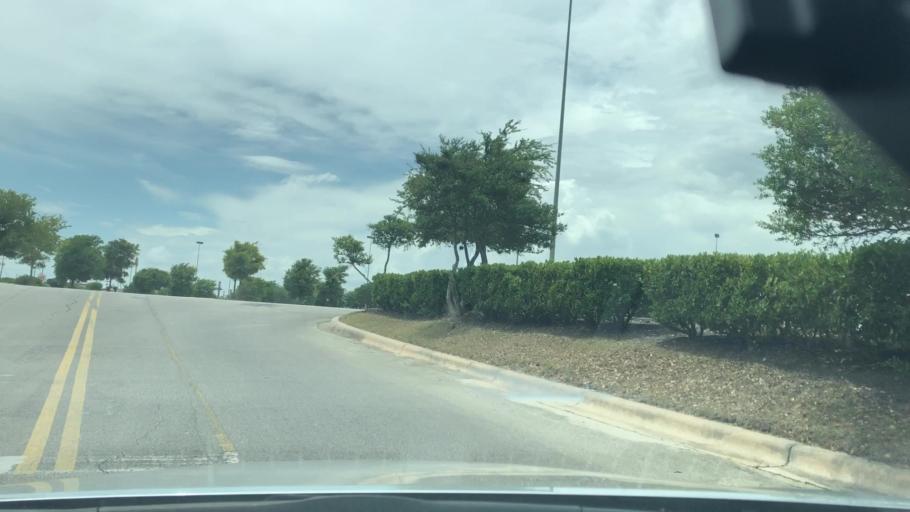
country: US
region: Texas
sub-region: Bexar County
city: Live Oak
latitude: 29.5950
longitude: -98.3478
